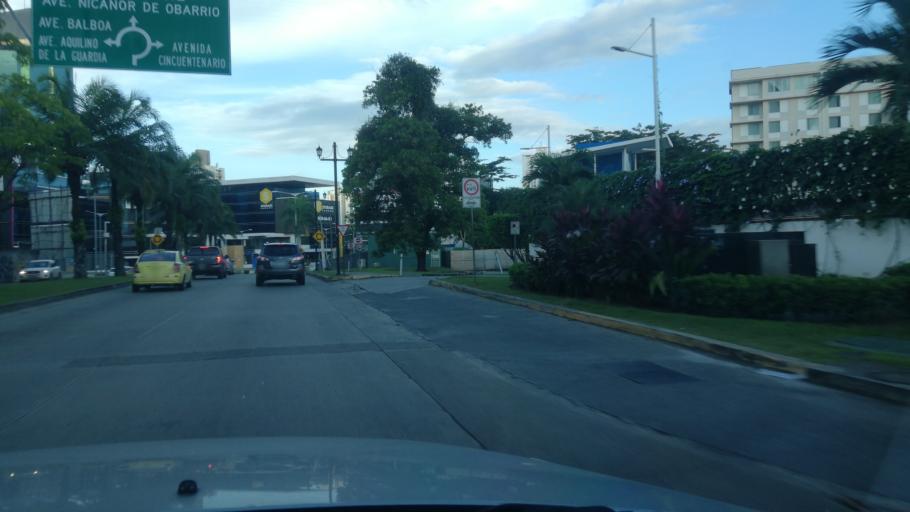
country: PA
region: Panama
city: Panama
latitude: 8.9836
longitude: -79.5120
